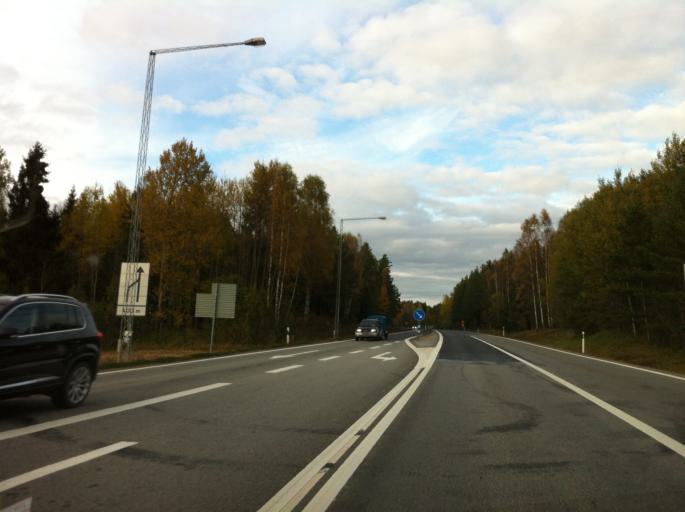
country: SE
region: OErebro
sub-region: Askersunds Kommun
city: Asbro
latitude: 58.9769
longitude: 15.0390
